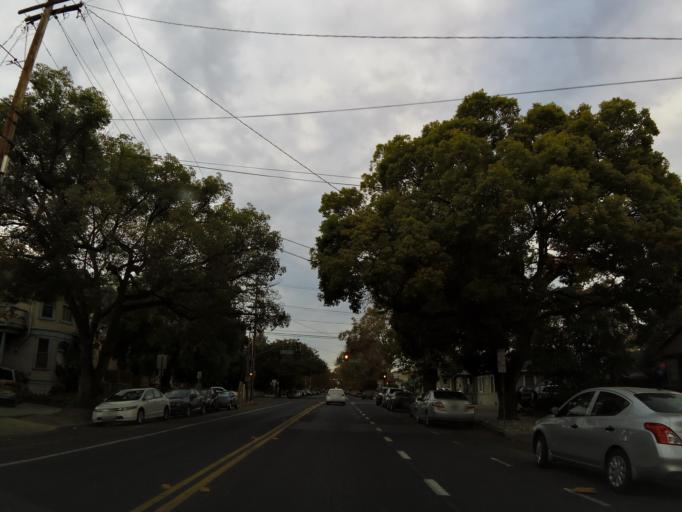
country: US
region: California
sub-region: Santa Clara County
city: San Jose
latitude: 37.3310
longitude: -121.8781
